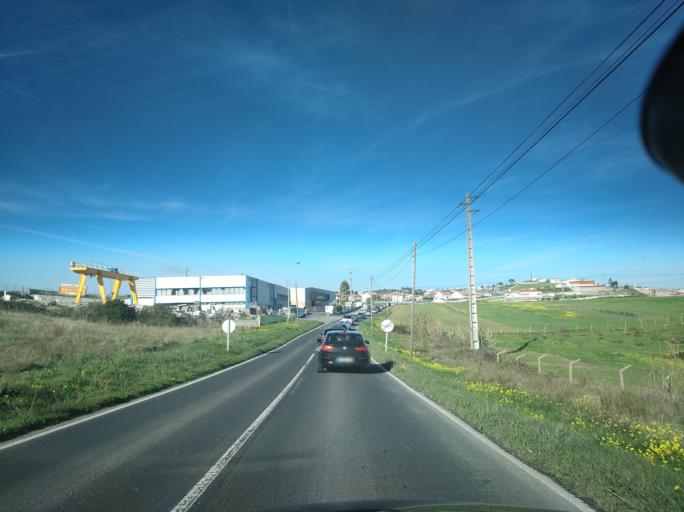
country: PT
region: Lisbon
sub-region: Mafra
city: Mafra
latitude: 38.9099
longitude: -9.3284
